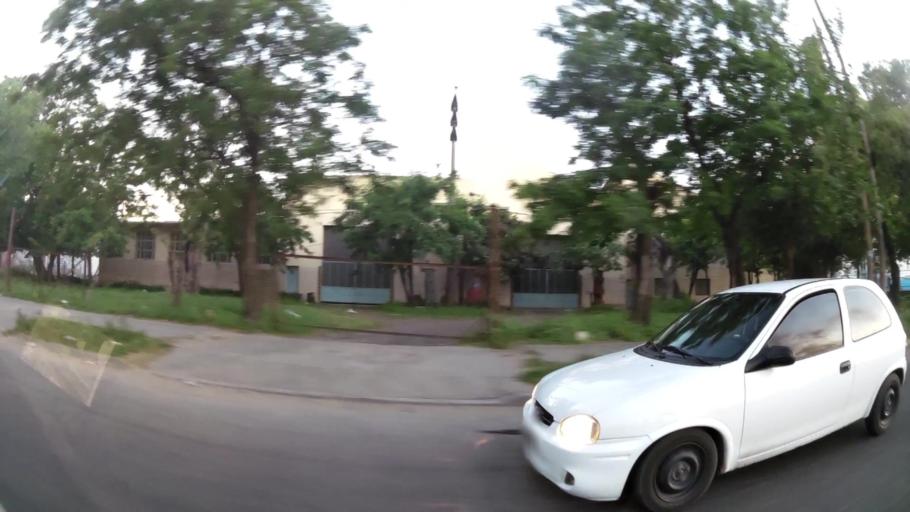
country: AR
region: Buenos Aires
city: San Justo
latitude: -34.7406
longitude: -58.6057
